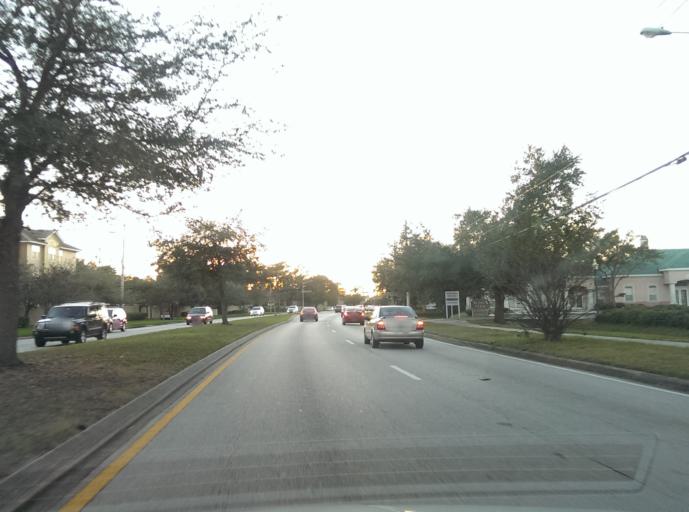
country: US
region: Florida
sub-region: Orange County
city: Oak Ridge
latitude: 28.4949
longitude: -81.4509
